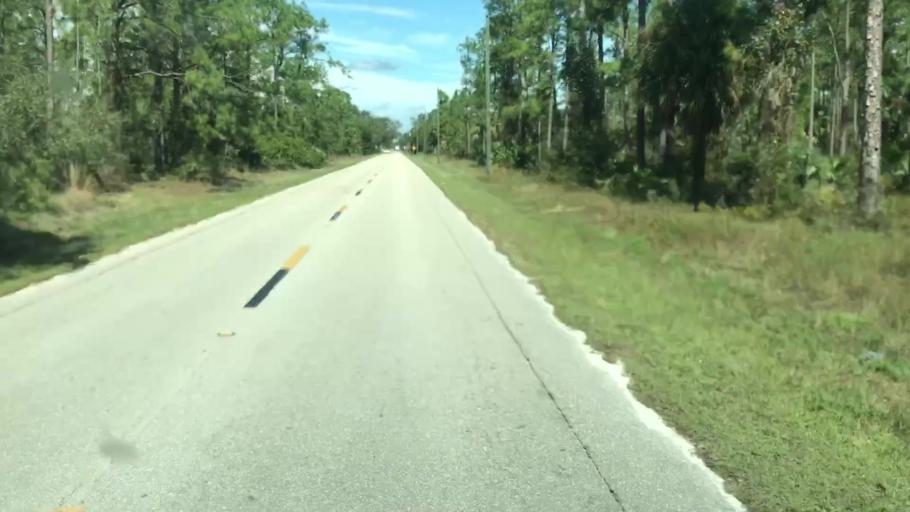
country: US
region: Florida
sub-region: Lee County
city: Lehigh Acres
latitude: 26.6474
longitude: -81.6465
